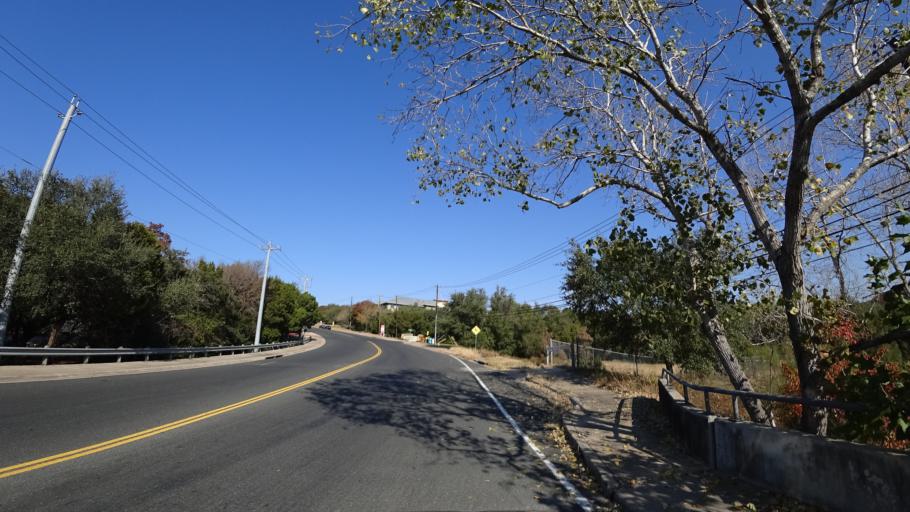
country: US
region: Texas
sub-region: Williamson County
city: Jollyville
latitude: 30.3866
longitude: -97.7673
